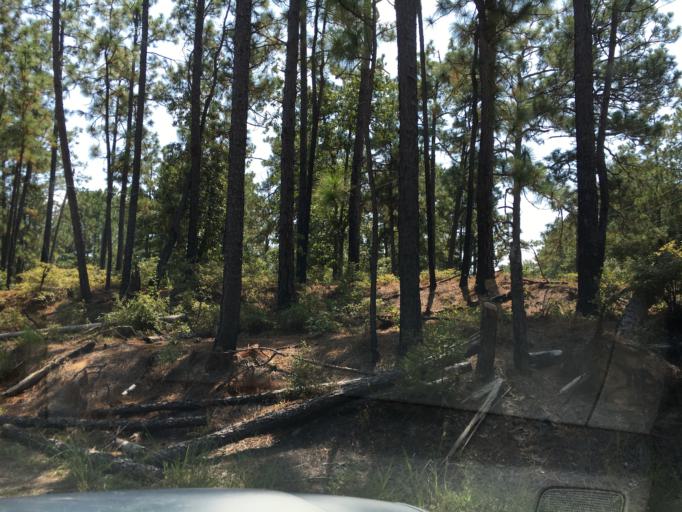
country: US
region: South Carolina
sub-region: Aiken County
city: New Ellenton
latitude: 33.4766
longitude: -81.6566
